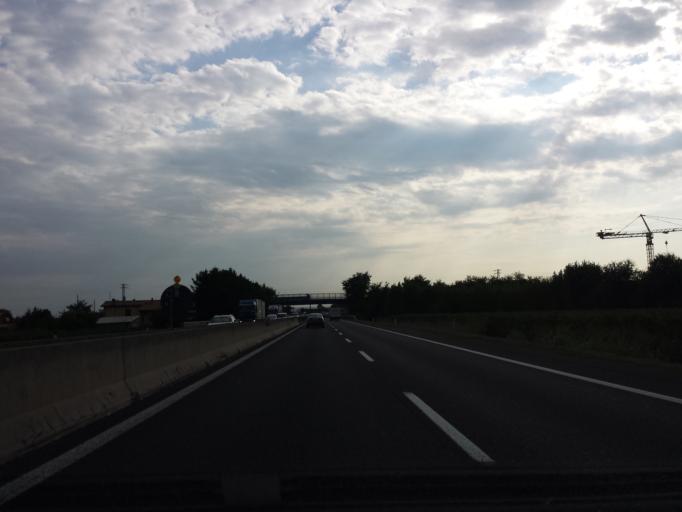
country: IT
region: Veneto
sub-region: Provincia di Padova
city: Terradura
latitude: 45.3275
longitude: 11.8346
